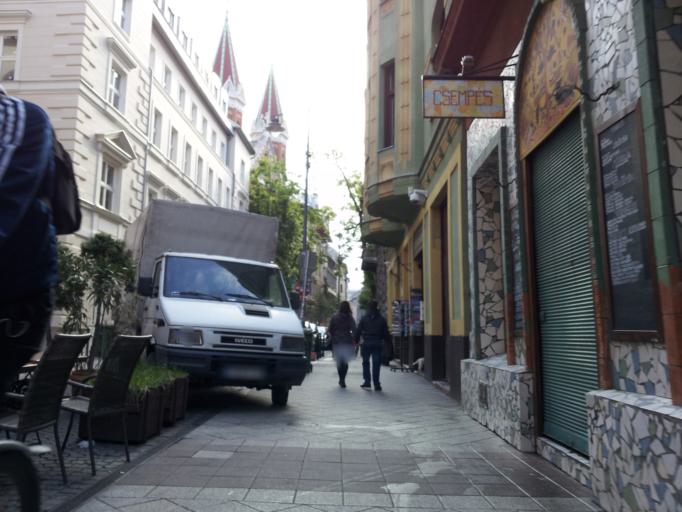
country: HU
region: Budapest
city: Budapest VIII. keruelet
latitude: 47.4906
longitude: 19.0674
